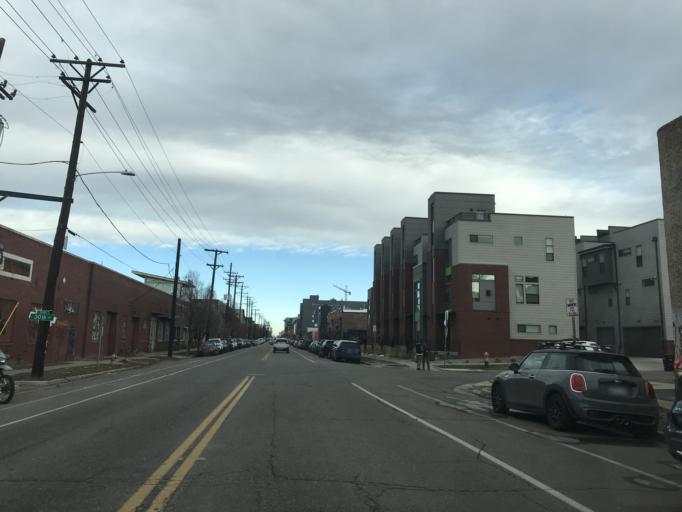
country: US
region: Colorado
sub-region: Denver County
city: Denver
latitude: 39.7635
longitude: -104.9825
